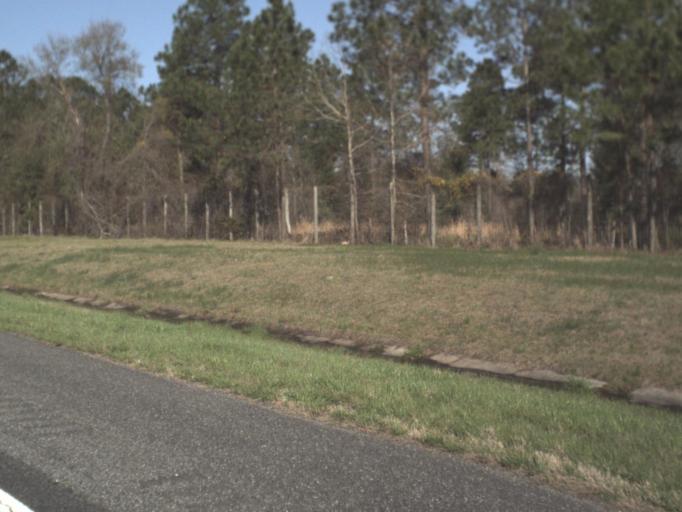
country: US
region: Florida
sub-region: Jefferson County
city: Monticello
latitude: 30.4782
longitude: -84.0697
